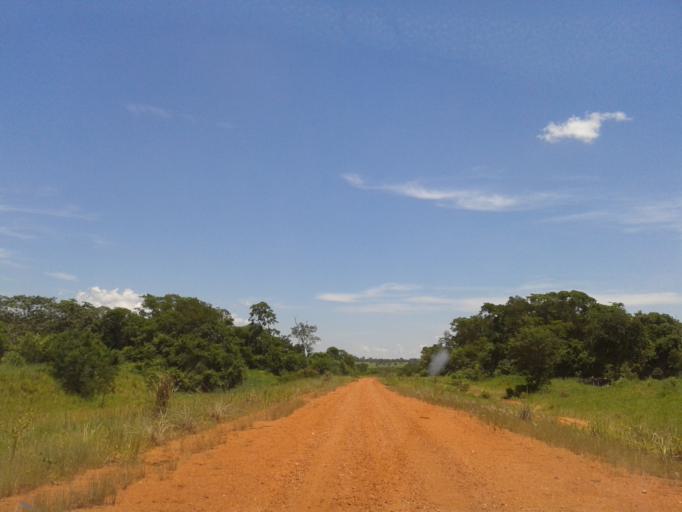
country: BR
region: Minas Gerais
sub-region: Santa Vitoria
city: Santa Vitoria
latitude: -19.1458
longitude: -50.5679
